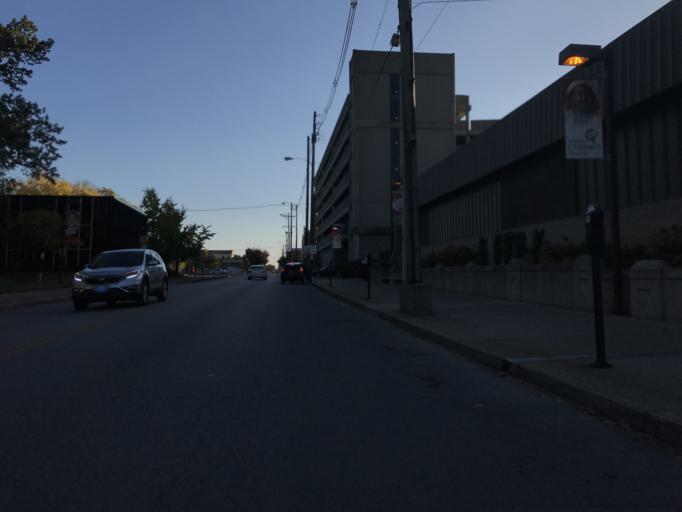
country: US
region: Kentucky
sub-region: Jefferson County
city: Louisville
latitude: 38.2451
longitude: -85.7498
